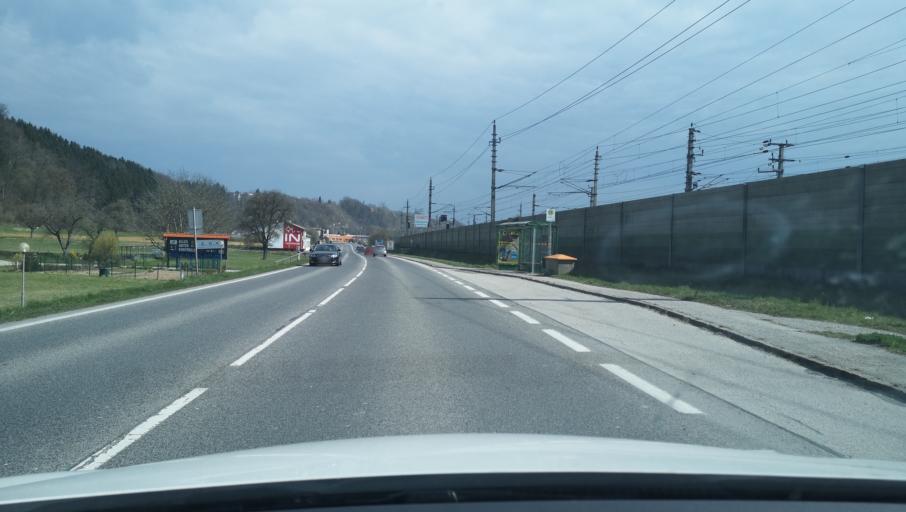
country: AT
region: Lower Austria
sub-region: Politischer Bezirk Amstetten
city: Amstetten
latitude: 48.1158
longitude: 14.8460
